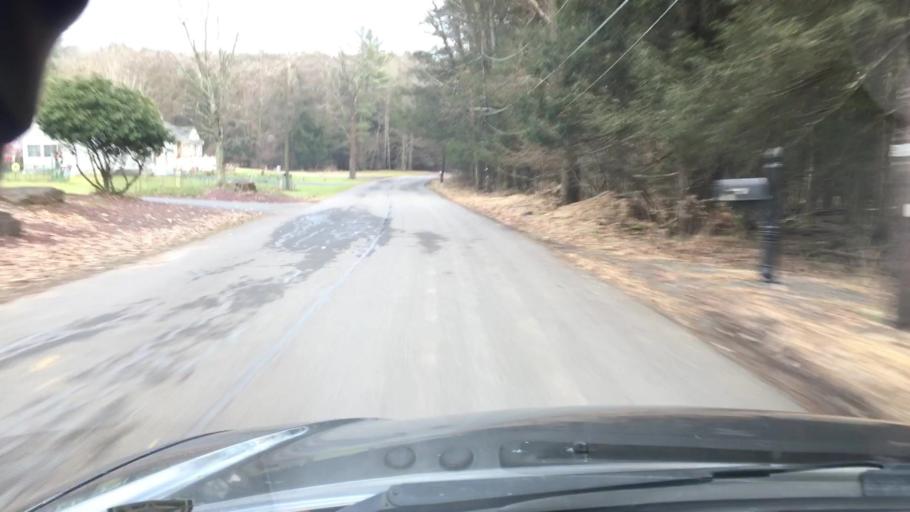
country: US
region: Pennsylvania
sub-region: Luzerne County
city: Back Mountain
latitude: 41.3101
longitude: -76.0620
